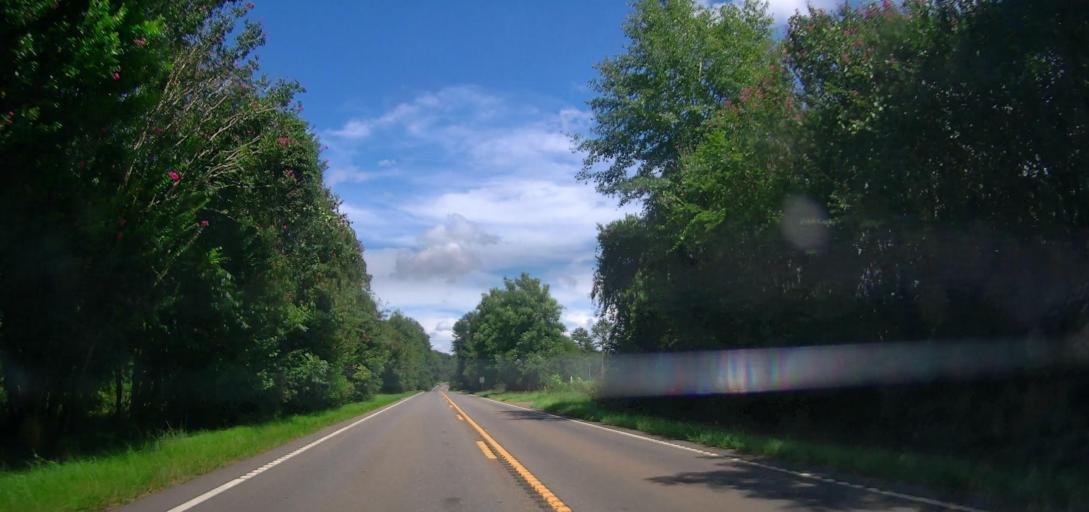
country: US
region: Georgia
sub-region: Macon County
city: Marshallville
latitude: 32.4541
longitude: -83.9605
